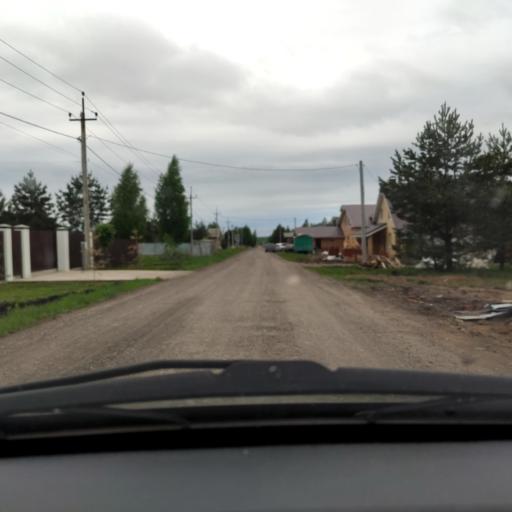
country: RU
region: Bashkortostan
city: Kabakovo
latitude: 54.6234
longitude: 56.1658
